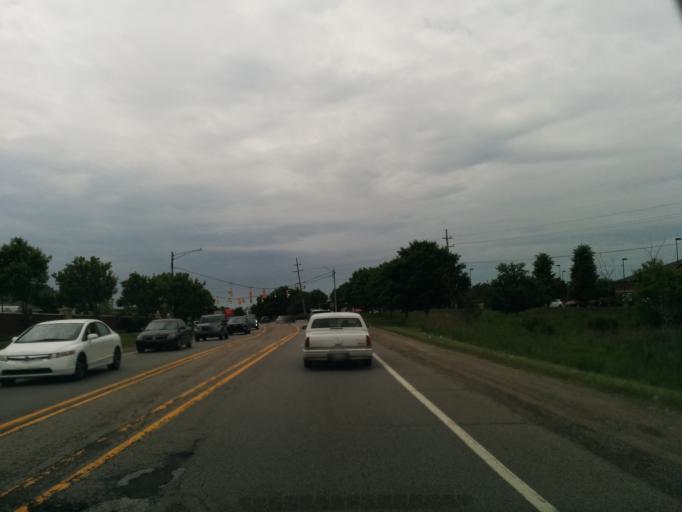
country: US
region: Michigan
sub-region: Oakland County
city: Wolverine Lake
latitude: 42.5364
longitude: -83.4370
